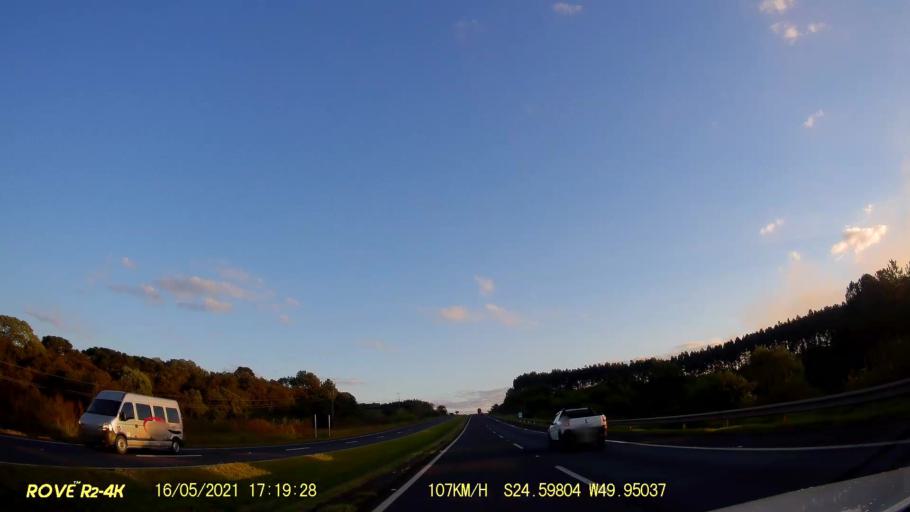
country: BR
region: Parana
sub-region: Pirai Do Sul
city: Pirai do Sul
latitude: -24.5984
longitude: -49.9506
